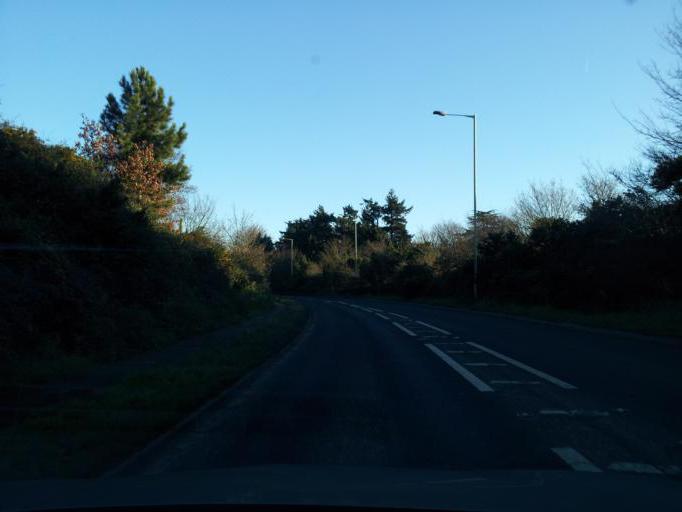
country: GB
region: England
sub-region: Suffolk
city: Woodbridge
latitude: 52.0844
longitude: 1.2925
